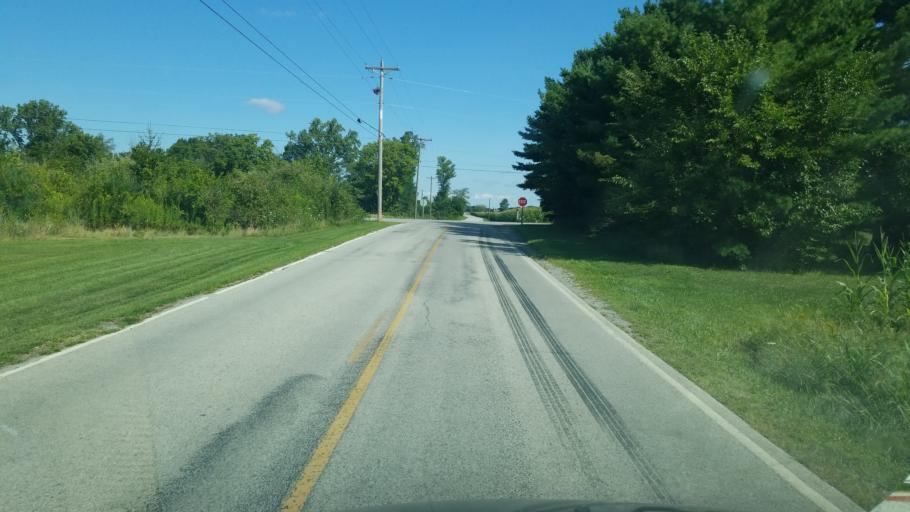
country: US
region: Ohio
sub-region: Wood County
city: North Baltimore
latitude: 41.1295
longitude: -83.7078
